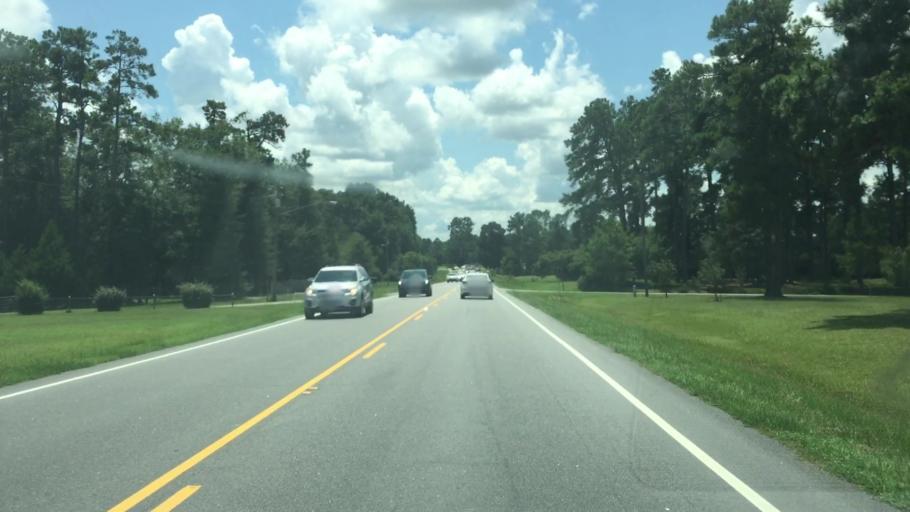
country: US
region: North Carolina
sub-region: Columbus County
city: Tabor City
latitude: 34.1649
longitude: -78.8450
